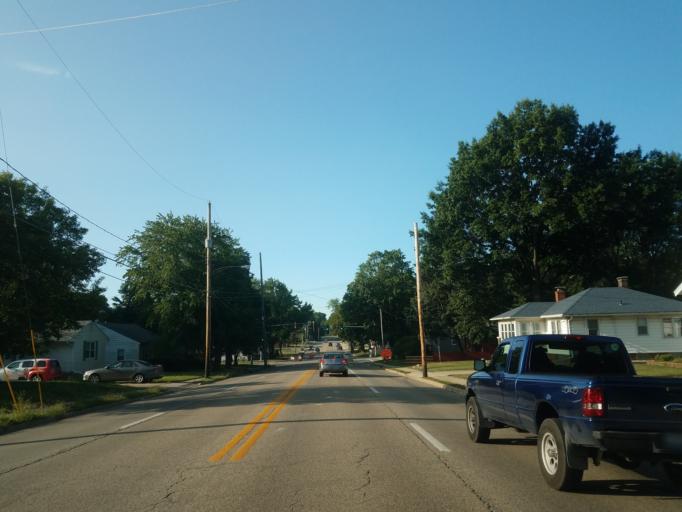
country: US
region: Illinois
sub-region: McLean County
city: Normal
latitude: 40.5058
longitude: -88.9823
